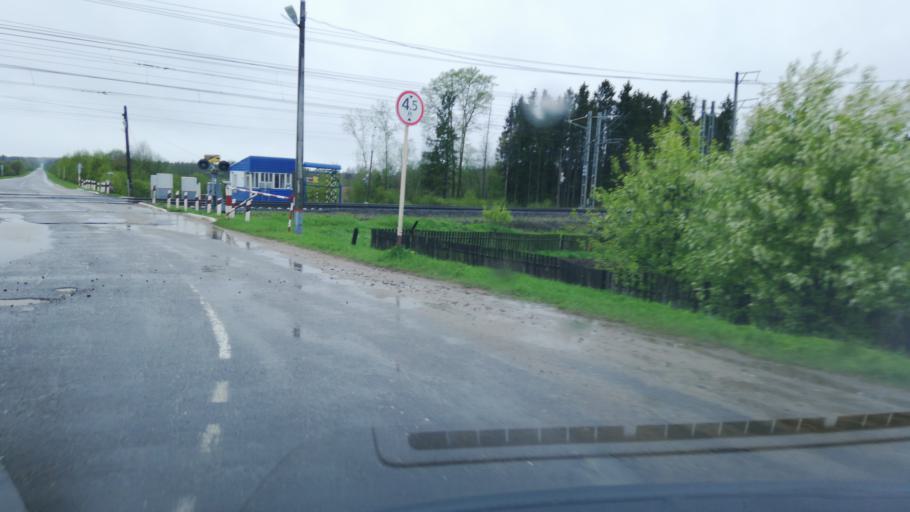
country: RU
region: Jaroslavl
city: Danilov
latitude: 58.0029
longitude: 40.1665
